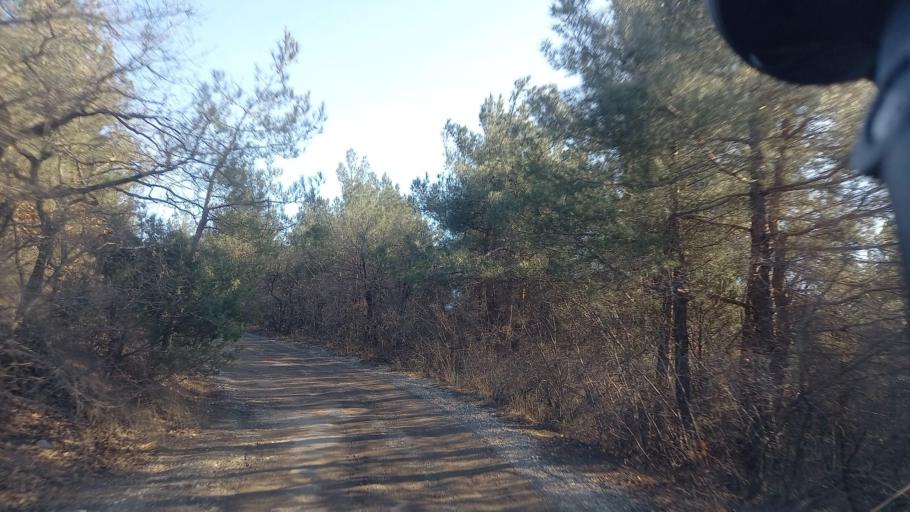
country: RU
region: Krasnodarskiy
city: Kabardinka
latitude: 44.6296
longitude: 37.9168
